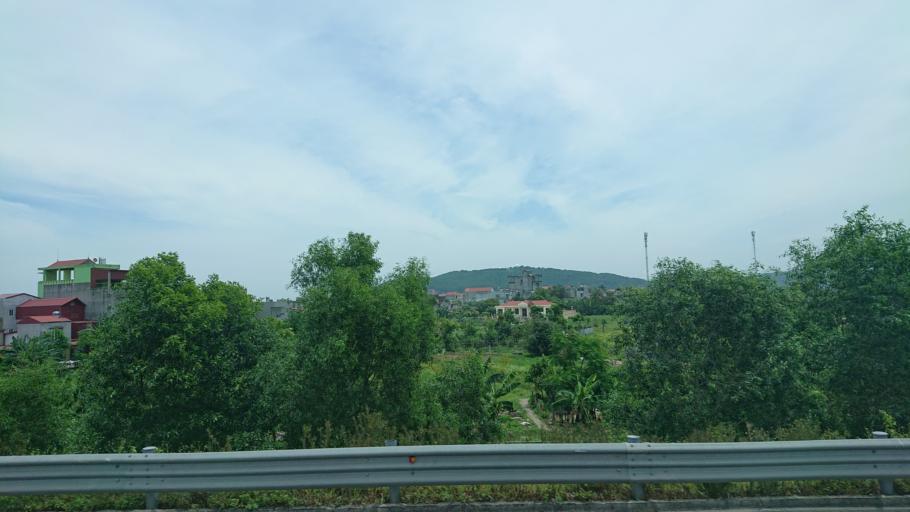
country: VN
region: Hai Phong
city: Nui Doi
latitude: 20.7708
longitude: 106.6115
